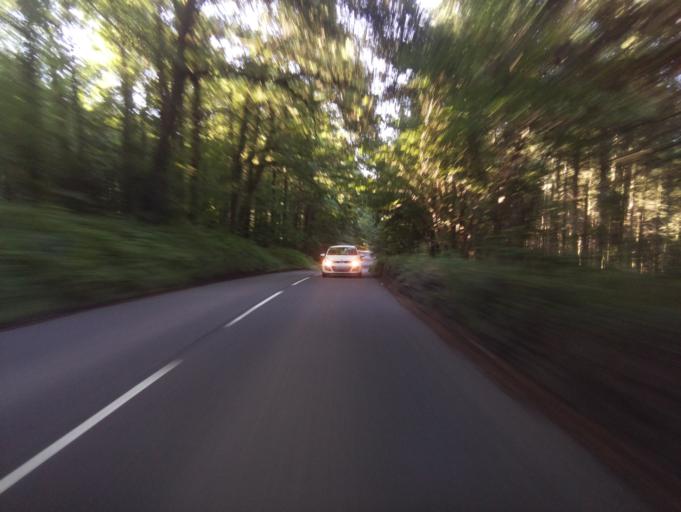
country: GB
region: Wales
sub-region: Monmouthshire
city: Tintern
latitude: 51.6711
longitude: -2.7497
